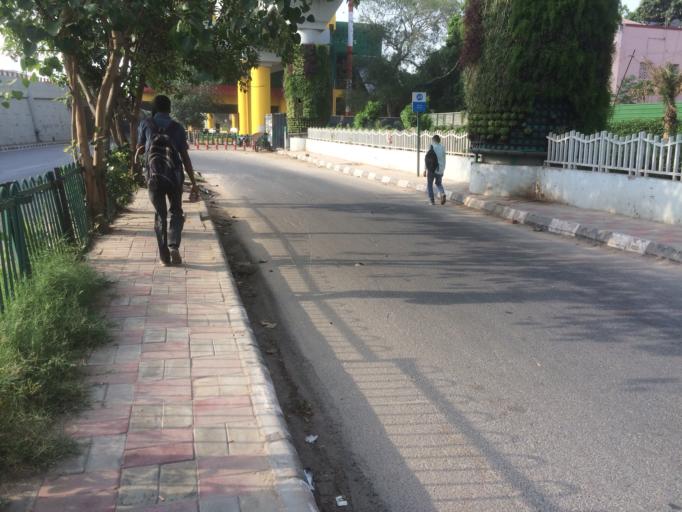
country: IN
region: NCT
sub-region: Central Delhi
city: Karol Bagh
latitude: 28.5797
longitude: 77.1751
